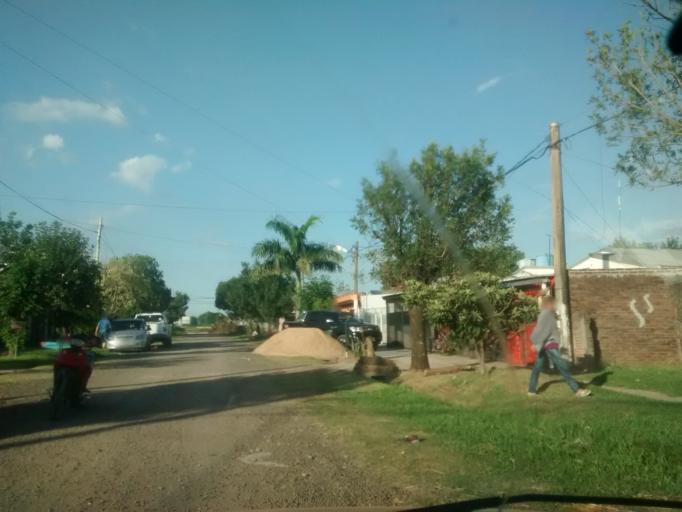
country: AR
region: Chaco
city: Fontana
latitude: -27.4495
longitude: -59.0223
